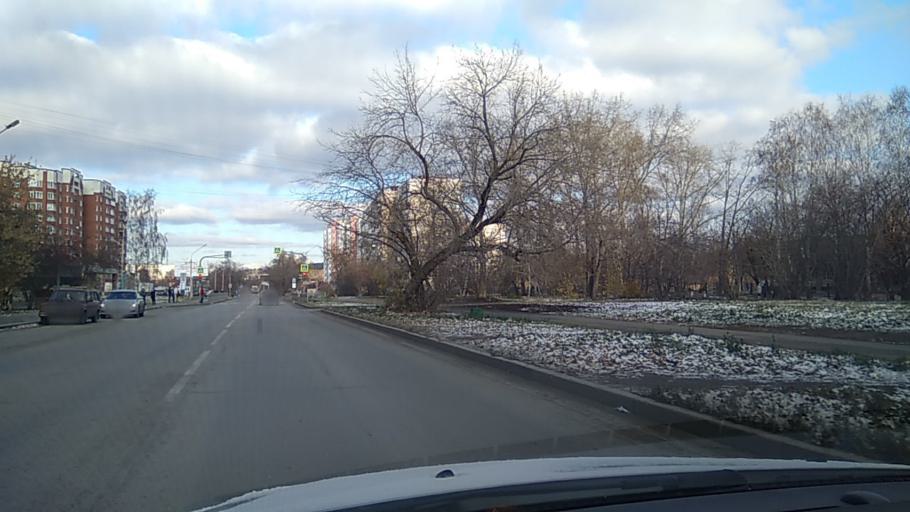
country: RU
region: Sverdlovsk
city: Sovkhoznyy
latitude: 56.7455
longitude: 60.6146
